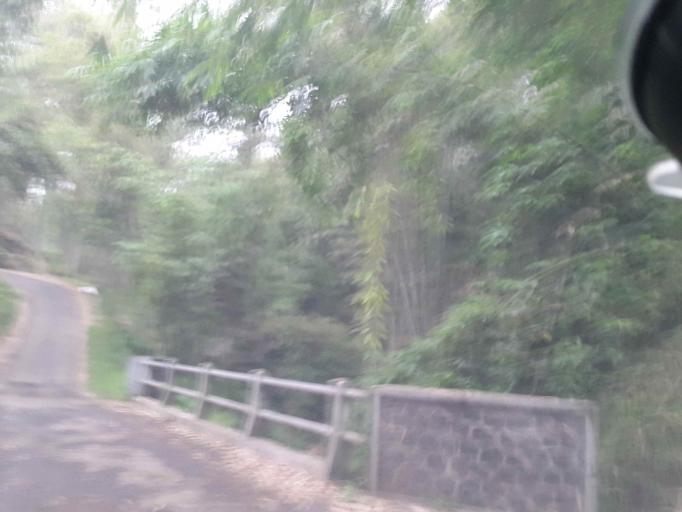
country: ID
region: East Java
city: Batu
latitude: -7.8109
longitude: 112.5325
